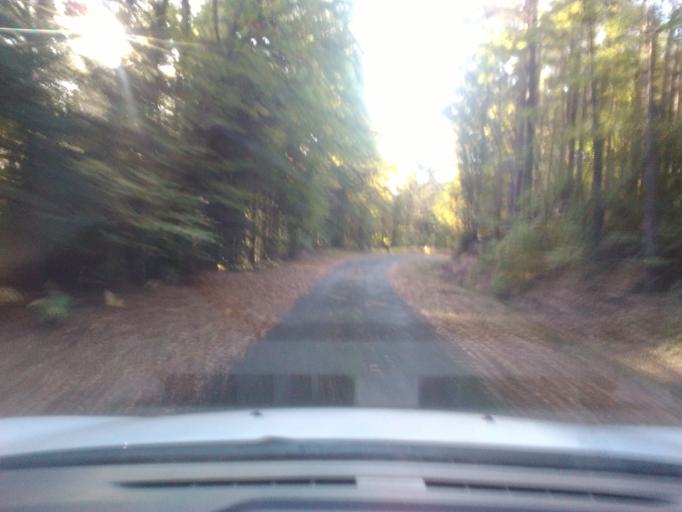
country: FR
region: Lorraine
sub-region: Departement des Vosges
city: Jeanmenil
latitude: 48.2859
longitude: 6.7202
